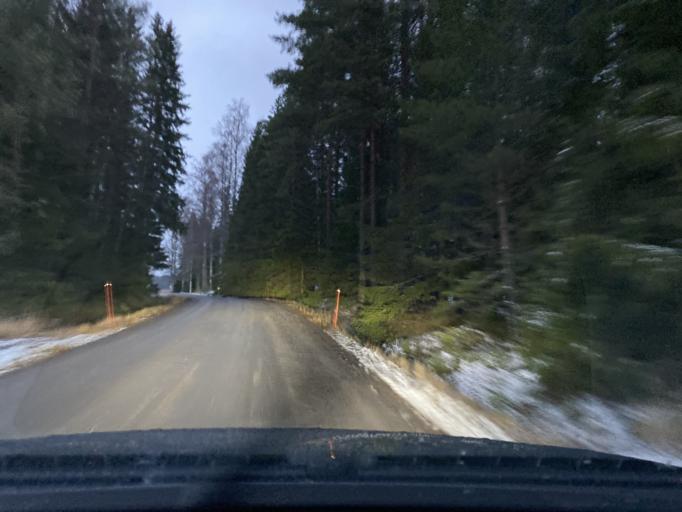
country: FI
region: Pirkanmaa
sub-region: Lounais-Pirkanmaa
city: Punkalaidun
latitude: 61.1613
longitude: 22.9460
